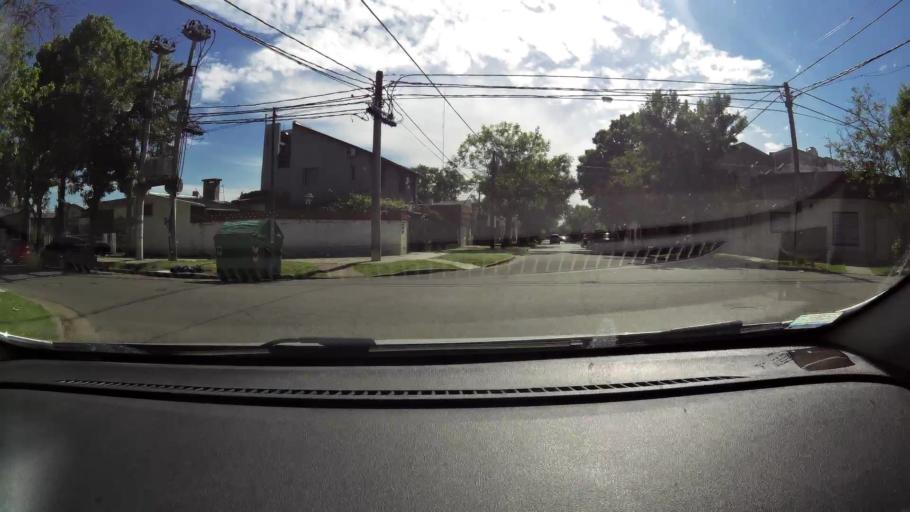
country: AR
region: Santa Fe
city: Granadero Baigorria
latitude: -32.9337
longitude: -60.7189
